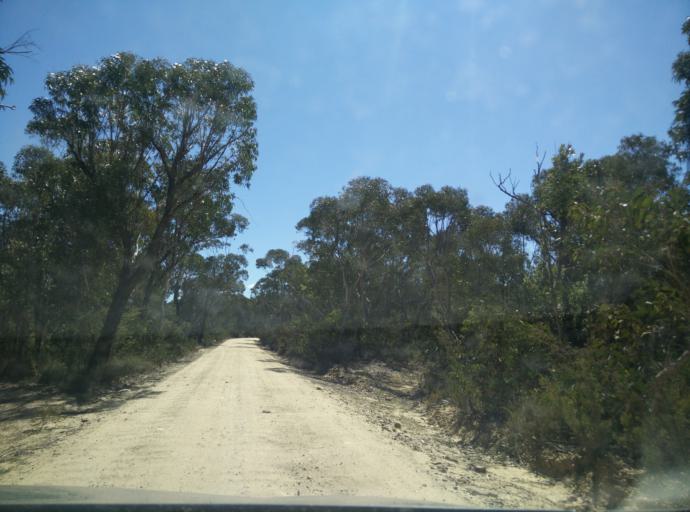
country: AU
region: New South Wales
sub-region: Blue Mountains Municipality
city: Blackheath
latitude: -33.5813
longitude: 150.2747
